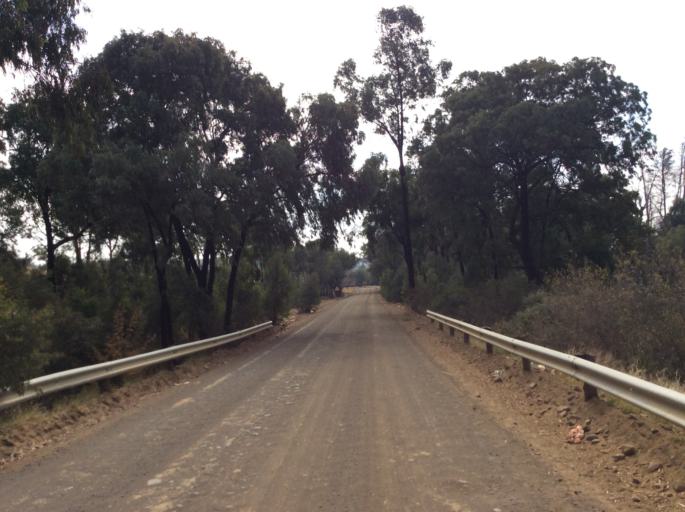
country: ZA
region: Orange Free State
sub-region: Xhariep District Municipality
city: Dewetsdorp
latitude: -29.5921
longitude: 26.6654
